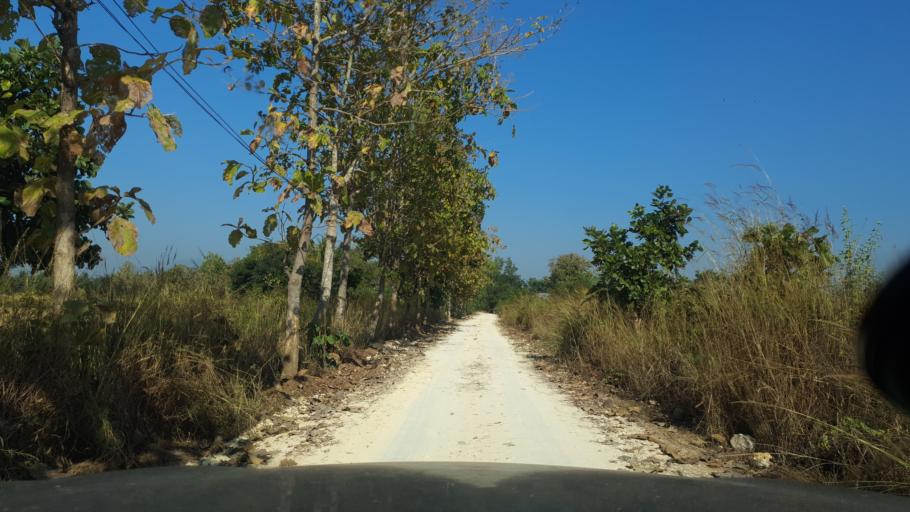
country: TH
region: Chiang Mai
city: San Kamphaeng
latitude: 18.7072
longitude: 99.0868
